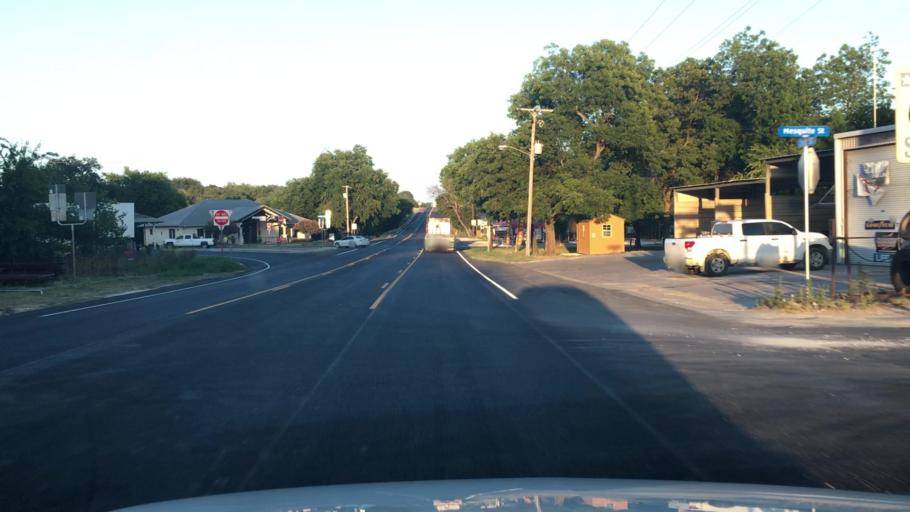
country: US
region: Texas
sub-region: Hamilton County
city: Hico
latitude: 31.9821
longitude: -98.0296
